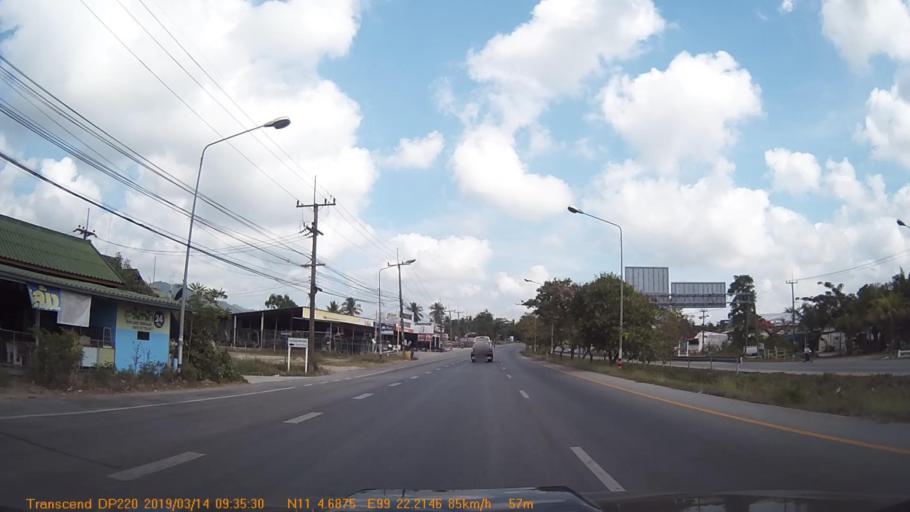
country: TH
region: Prachuap Khiri Khan
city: Bang Saphan Noi
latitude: 11.0789
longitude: 99.3699
